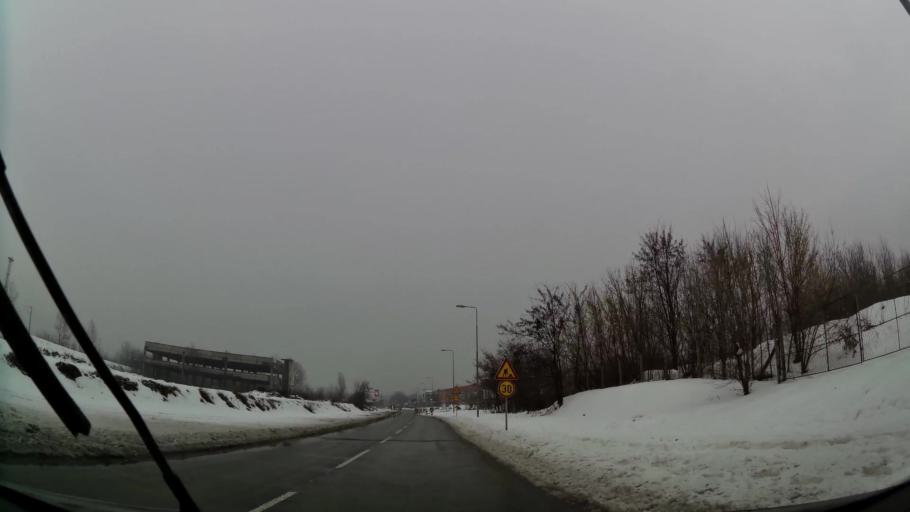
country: RS
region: Central Serbia
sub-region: Belgrade
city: Zemun
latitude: 44.8381
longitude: 20.3581
